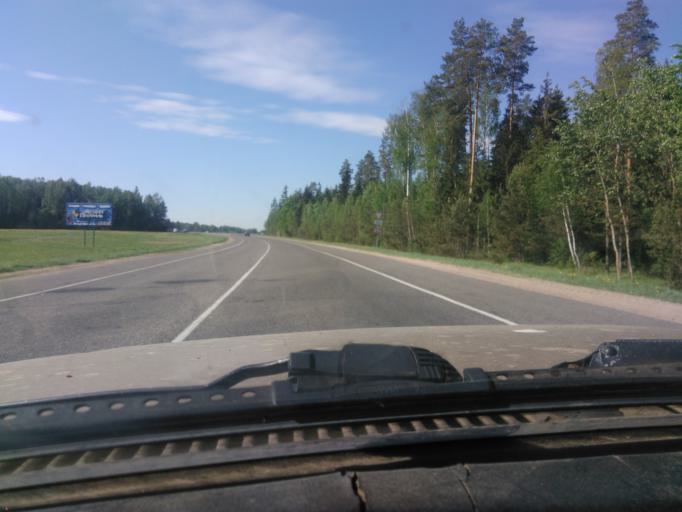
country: BY
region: Mogilev
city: Myazhysyatki
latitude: 53.8048
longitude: 30.2075
